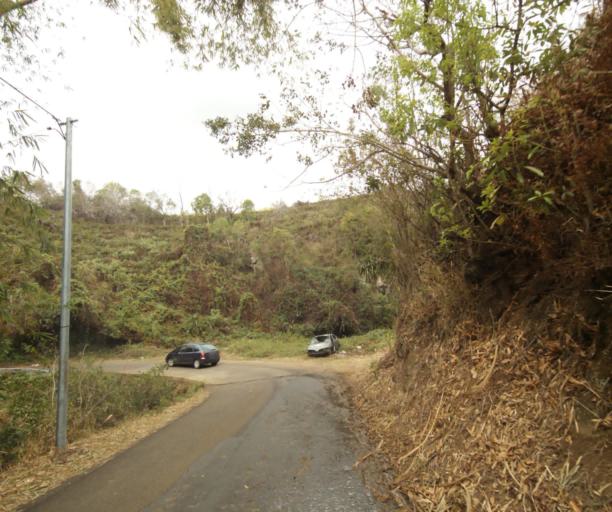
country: RE
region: Reunion
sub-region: Reunion
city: Saint-Paul
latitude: -21.0293
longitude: 55.3018
